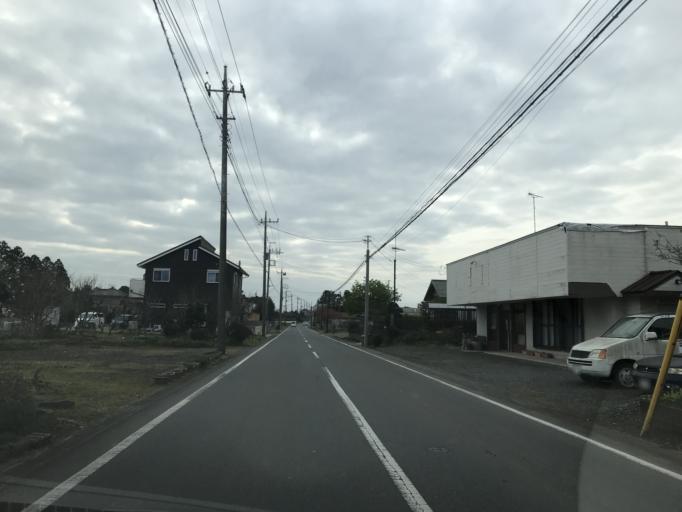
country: JP
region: Chiba
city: Omigawa
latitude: 35.8010
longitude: 140.5576
